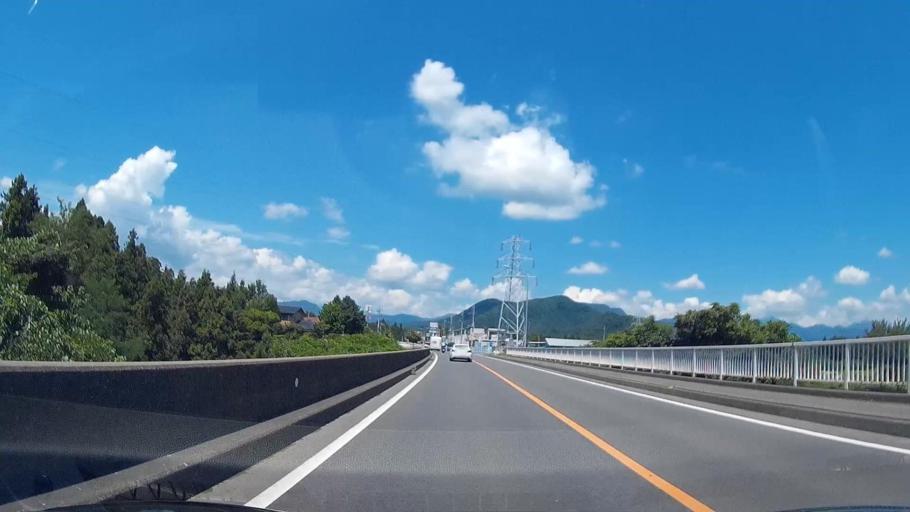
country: JP
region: Gunma
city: Numata
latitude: 36.6714
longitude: 138.9876
